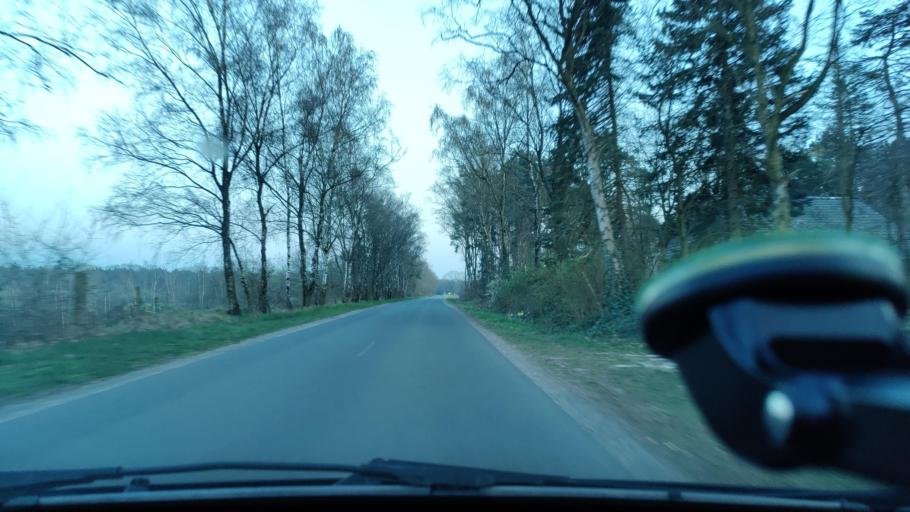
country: NL
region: Limburg
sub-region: Gemeente Bergen
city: Wellerlooi
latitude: 51.5303
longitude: 6.1866
